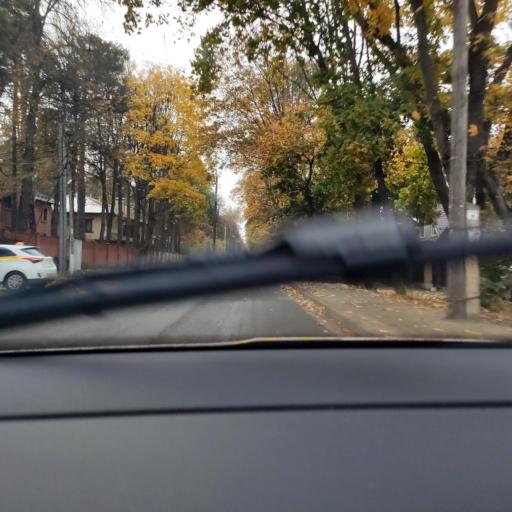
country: RU
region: Moskovskaya
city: Mamontovka
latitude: 55.9801
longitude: 37.8370
